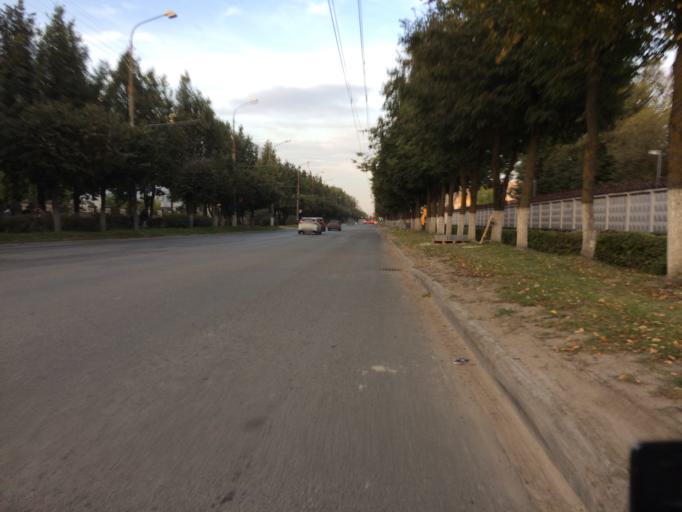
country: RU
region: Mariy-El
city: Yoshkar-Ola
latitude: 56.6344
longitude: 47.8591
